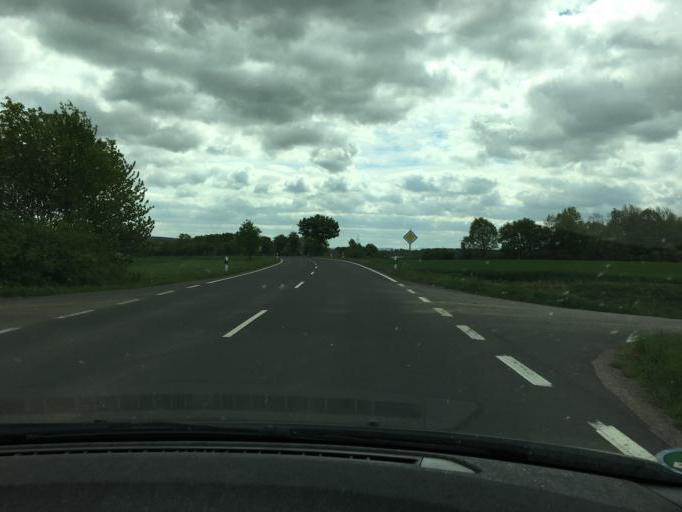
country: DE
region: North Rhine-Westphalia
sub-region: Regierungsbezirk Koln
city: Mechernich
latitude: 50.6371
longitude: 6.6767
